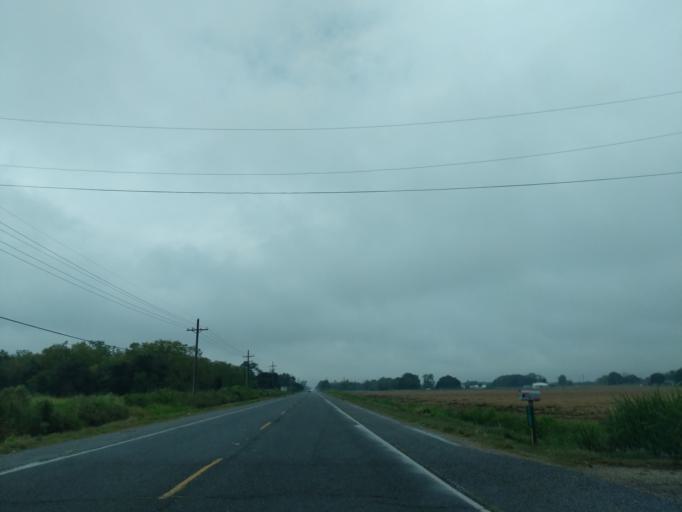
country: US
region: Louisiana
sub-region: Vermilion Parish
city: Abbeville
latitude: 29.9914
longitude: -92.2010
